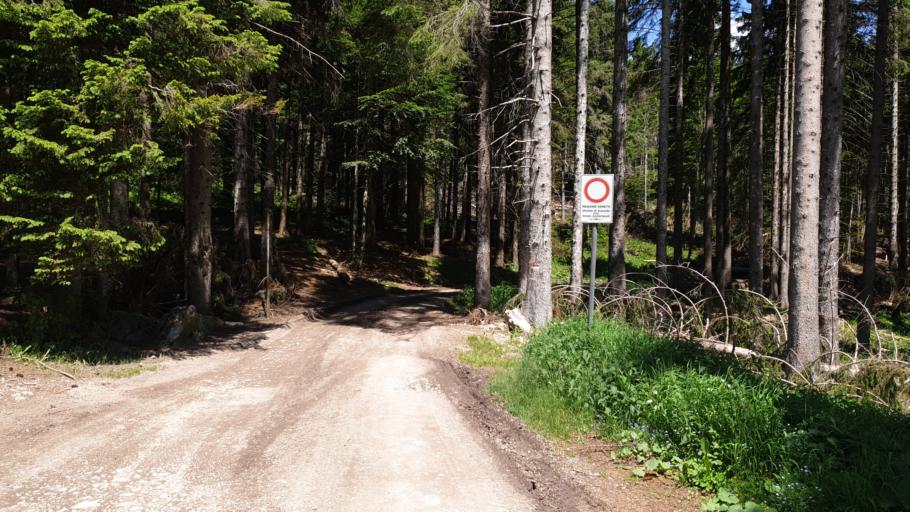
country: IT
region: Veneto
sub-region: Provincia di Vicenza
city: Canove di Roana
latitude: 45.8974
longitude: 11.4814
